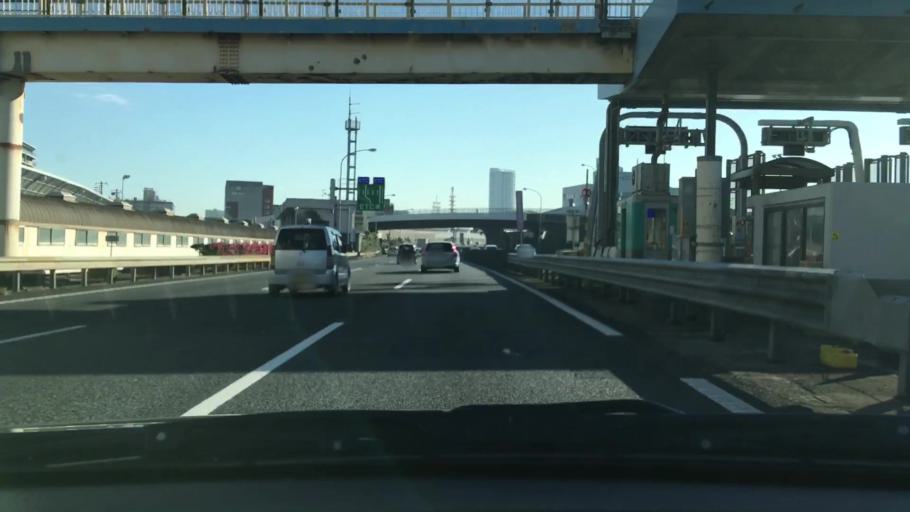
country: JP
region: Chiba
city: Funabashi
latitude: 35.6995
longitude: 139.9661
